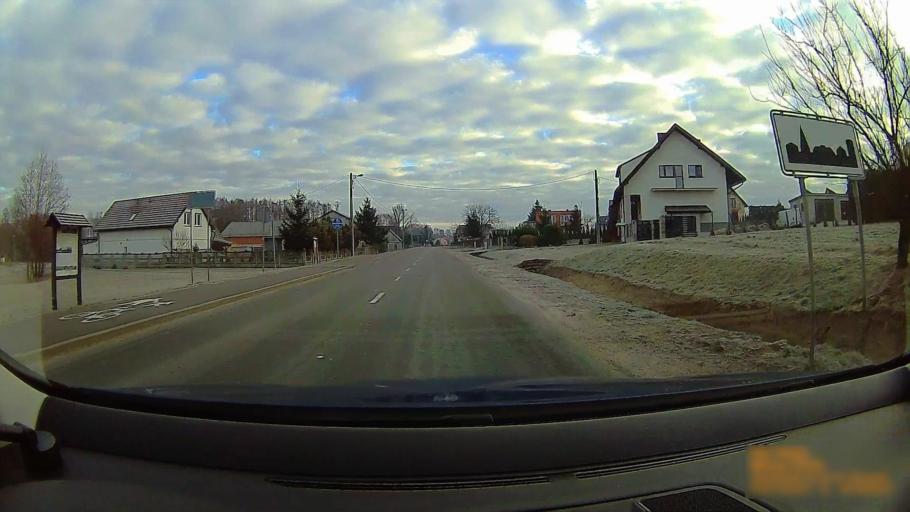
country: PL
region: Greater Poland Voivodeship
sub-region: Powiat koninski
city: Rzgow Pierwszy
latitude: 52.1749
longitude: 18.0932
